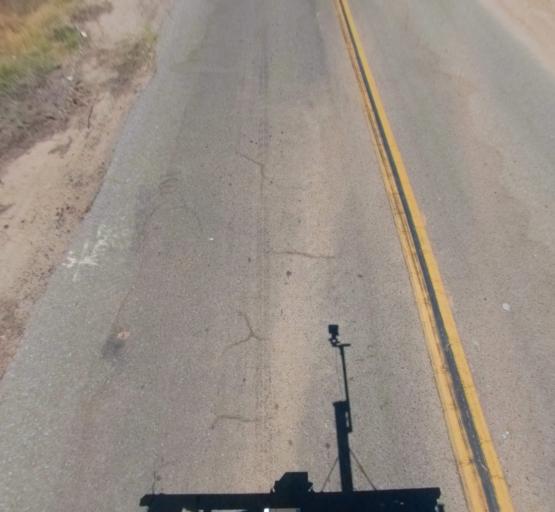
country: US
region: California
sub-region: Madera County
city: Madera Acres
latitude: 37.0980
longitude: -120.0757
